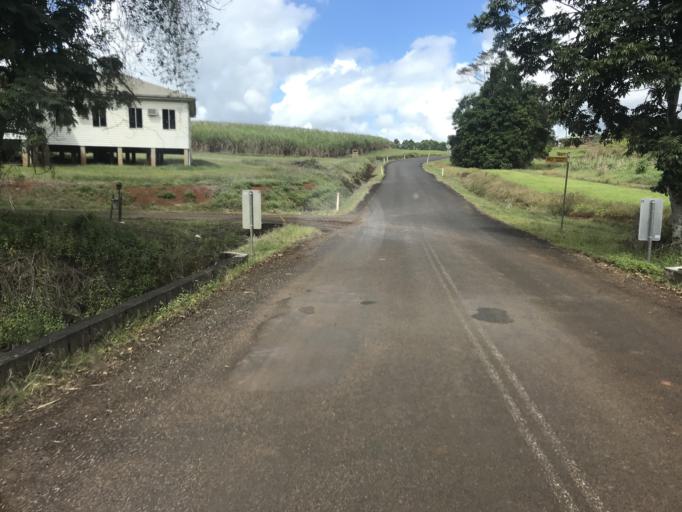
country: AU
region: Queensland
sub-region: Cassowary Coast
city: Innisfail
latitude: -17.5508
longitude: 145.8802
